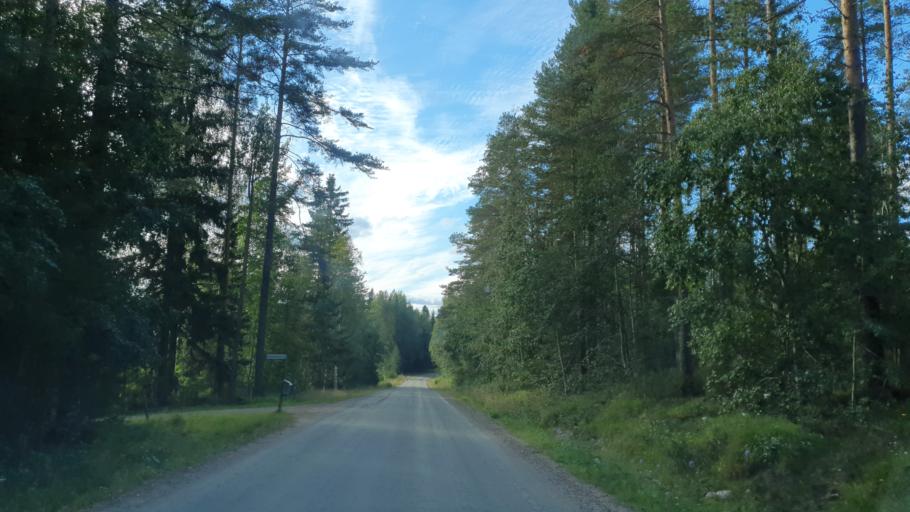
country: FI
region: Kainuu
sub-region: Kehys-Kainuu
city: Kuhmo
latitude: 64.1655
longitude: 29.4501
